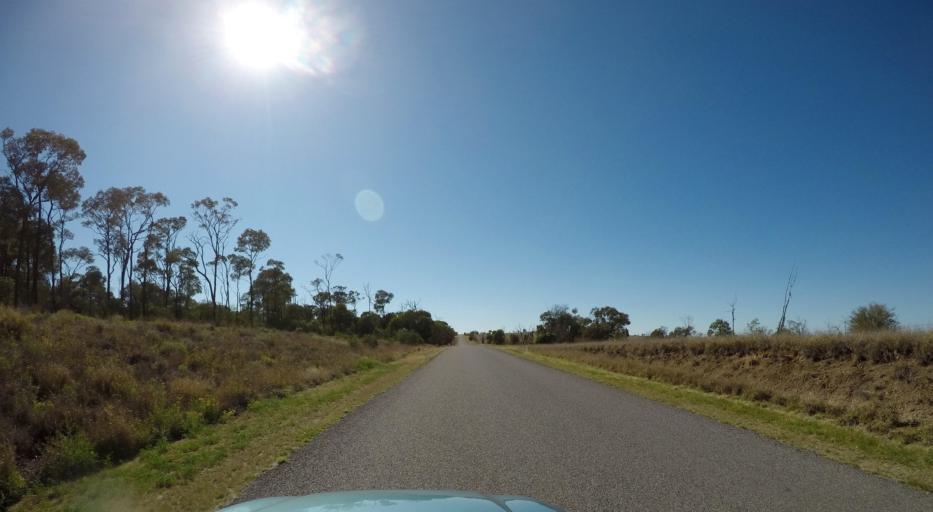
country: AU
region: Queensland
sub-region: Banana
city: Taroom
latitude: -25.7886
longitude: 149.6795
